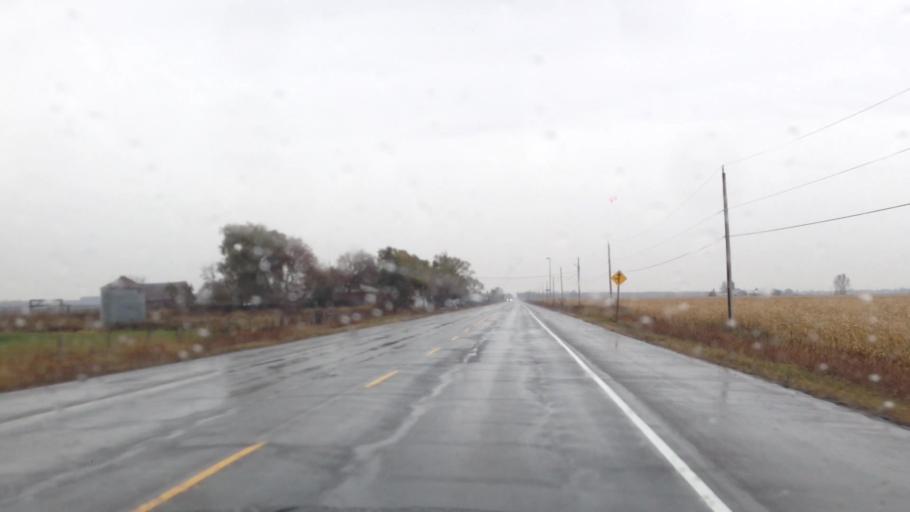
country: CA
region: Ontario
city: Clarence-Rockland
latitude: 45.4609
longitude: -75.4299
